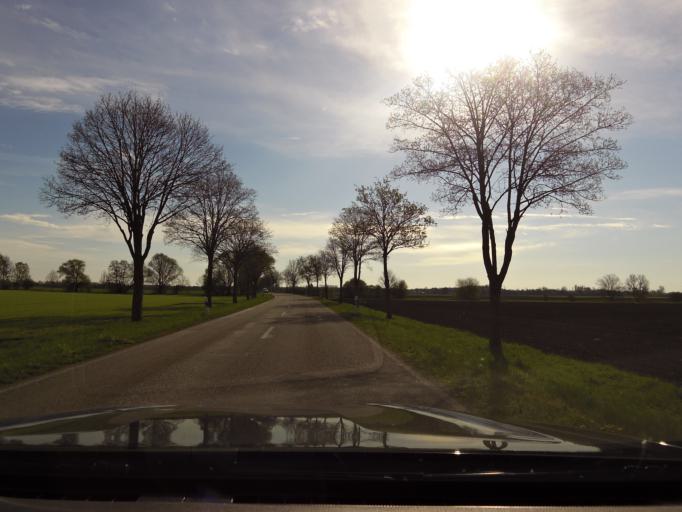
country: DE
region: Bavaria
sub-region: Upper Bavaria
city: Hallbergmoos
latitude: 48.3342
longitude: 11.7680
